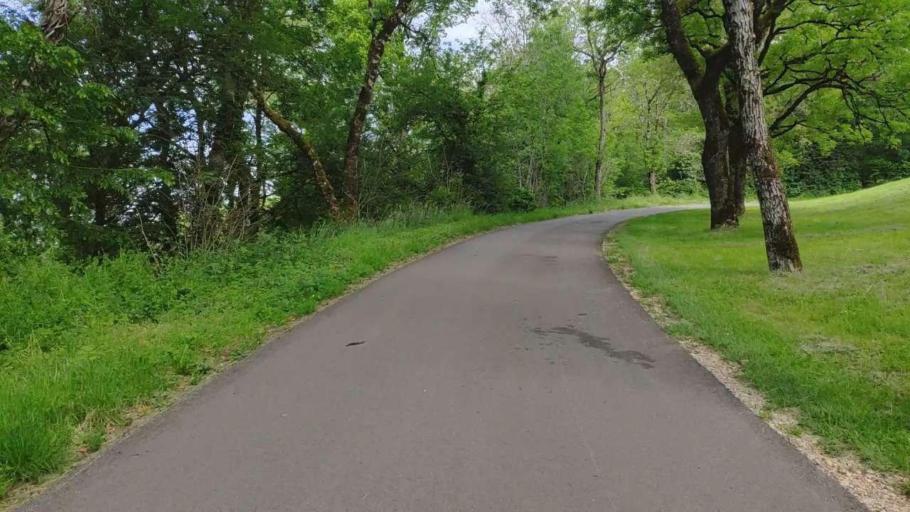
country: FR
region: Franche-Comte
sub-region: Departement du Jura
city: Poligny
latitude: 46.7743
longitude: 5.6237
